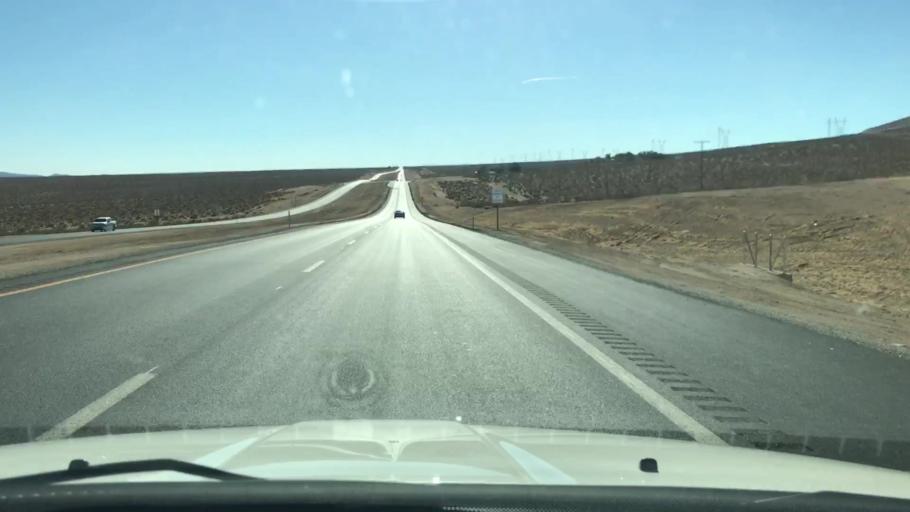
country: US
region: California
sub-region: Kern County
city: Inyokern
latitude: 35.6254
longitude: -117.8877
